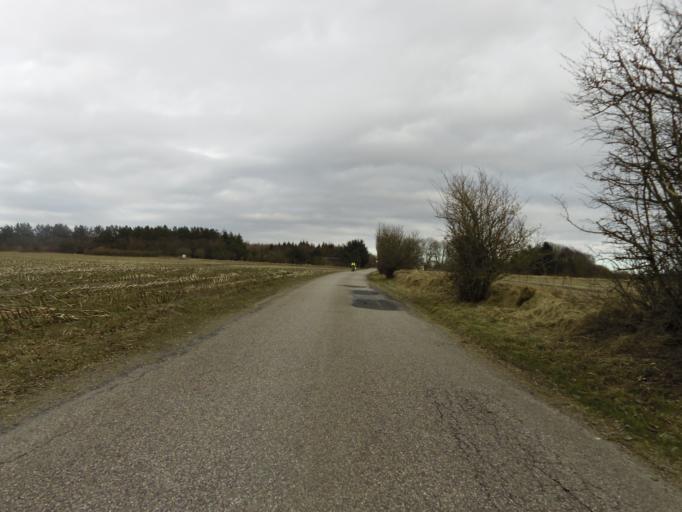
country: DK
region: South Denmark
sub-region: Tonder Kommune
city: Toftlund
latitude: 55.2068
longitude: 9.1869
